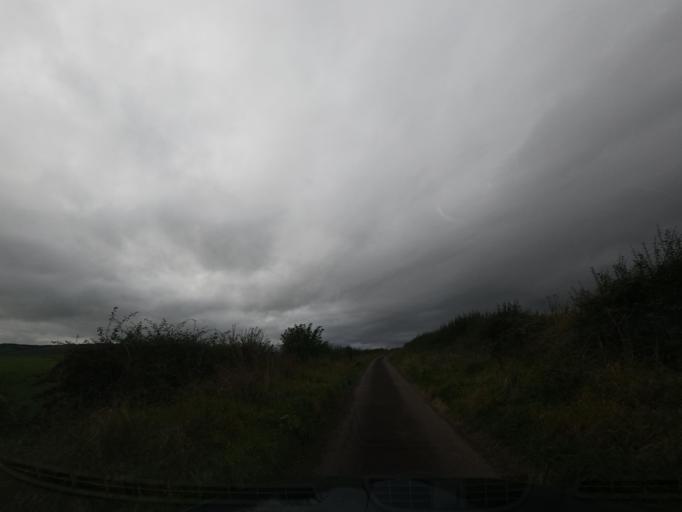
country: GB
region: England
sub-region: Northumberland
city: Ford
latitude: 55.6088
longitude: -2.0588
